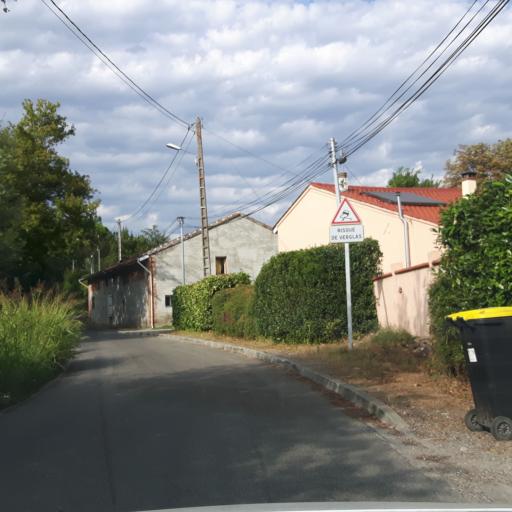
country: FR
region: Midi-Pyrenees
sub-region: Departement de la Haute-Garonne
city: Castelnau-d'Estretefonds
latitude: 43.7788
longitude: 1.3677
